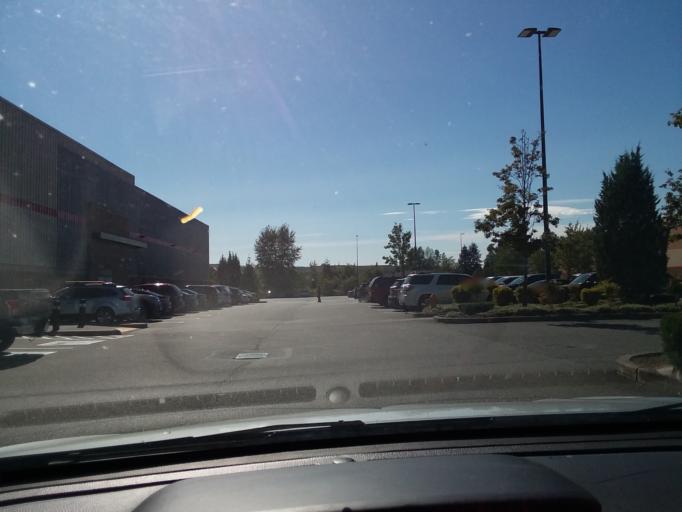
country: US
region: Washington
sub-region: Snohomish County
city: Smokey Point
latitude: 48.1480
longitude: -122.1918
